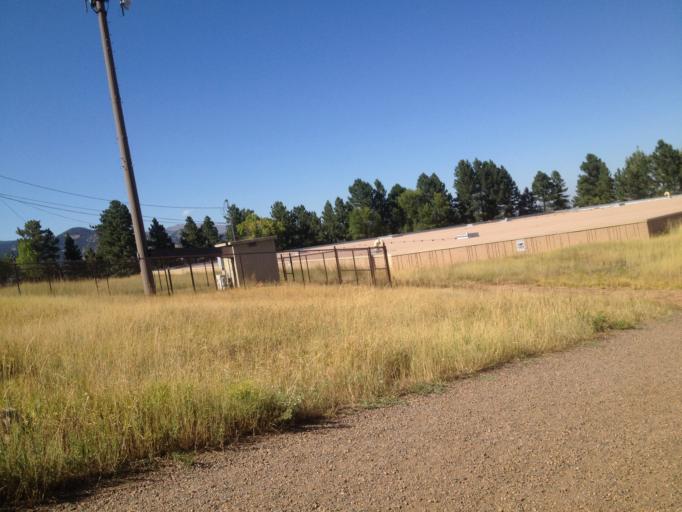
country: US
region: Colorado
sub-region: Boulder County
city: Boulder
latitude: 39.9939
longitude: -105.2792
